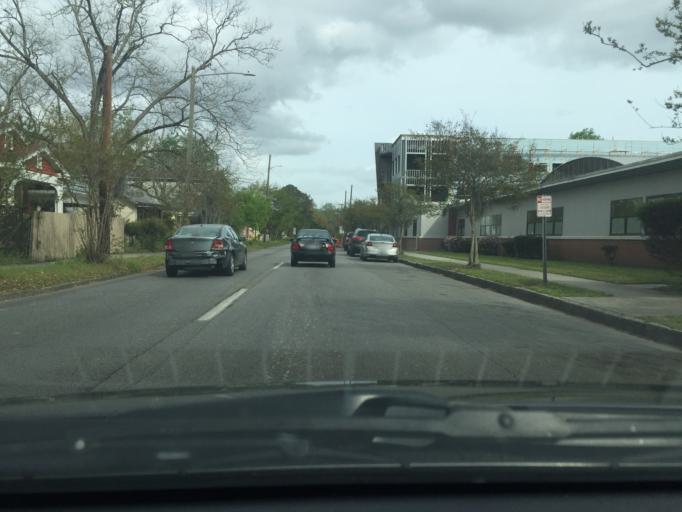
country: US
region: Georgia
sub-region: Chatham County
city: Savannah
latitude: 32.0597
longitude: -81.0879
